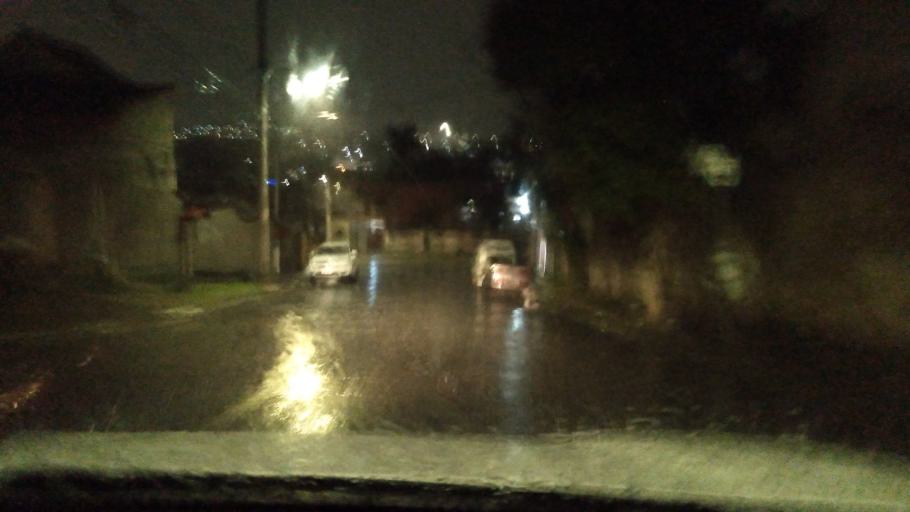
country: BR
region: Minas Gerais
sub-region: Belo Horizonte
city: Belo Horizonte
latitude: -19.8812
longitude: -43.9411
